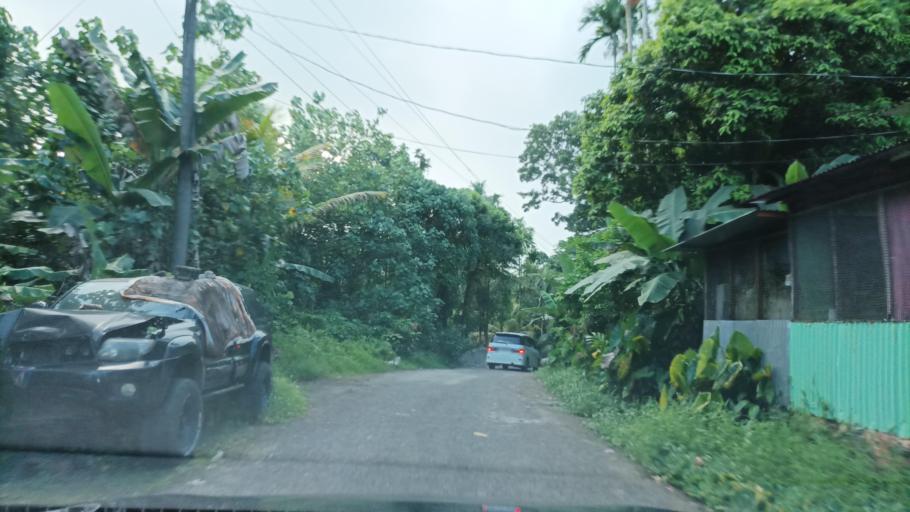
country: FM
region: Pohnpei
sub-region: Madolenihm Municipality
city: Madolenihm Municipality Government
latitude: 6.8446
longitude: 158.3046
